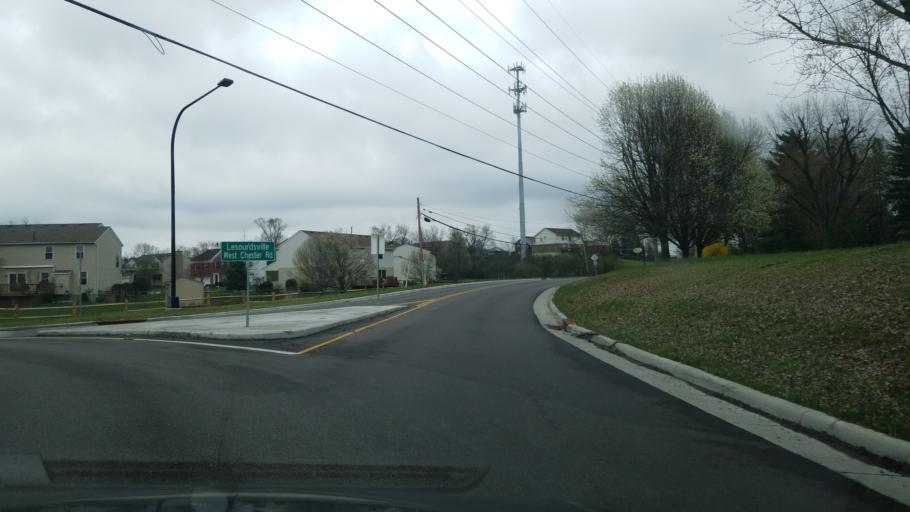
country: US
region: Ohio
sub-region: Butler County
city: Beckett Ridge
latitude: 39.3721
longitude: -84.4251
